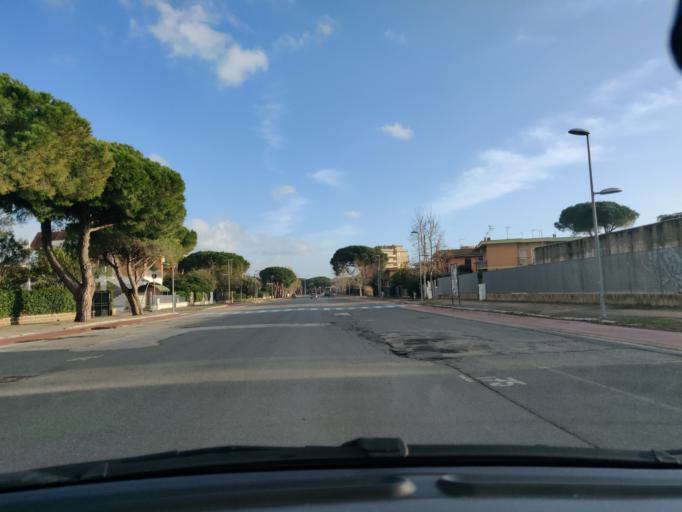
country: IT
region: Latium
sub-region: Provincia di Viterbo
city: Tarquinia
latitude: 42.2238
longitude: 11.7077
